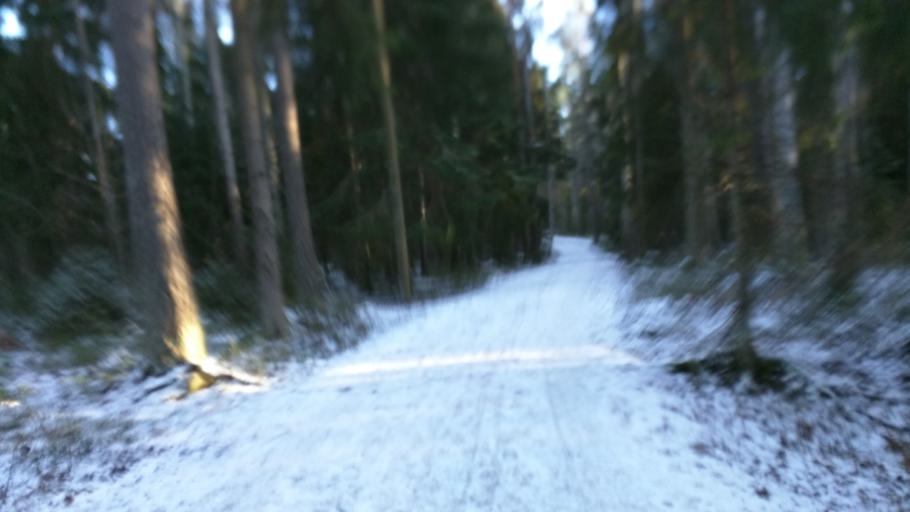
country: FI
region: Uusimaa
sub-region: Helsinki
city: Kauniainen
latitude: 60.2147
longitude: 24.6988
